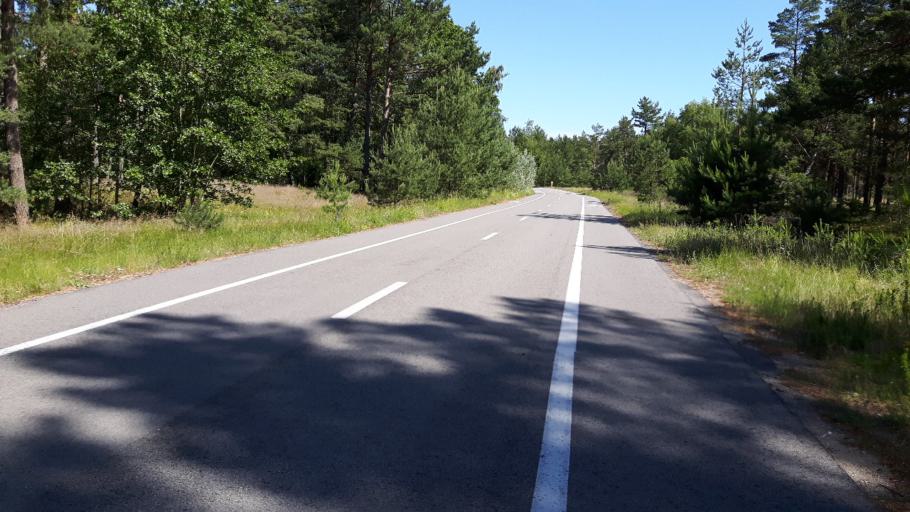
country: LT
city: Nida
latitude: 55.3240
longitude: 21.0258
